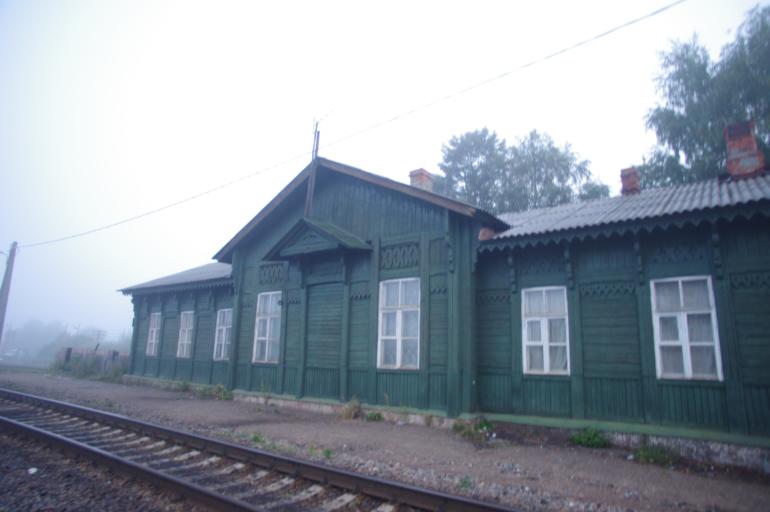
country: RU
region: Jaroslavl
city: Borok
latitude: 57.9316
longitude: 38.2409
